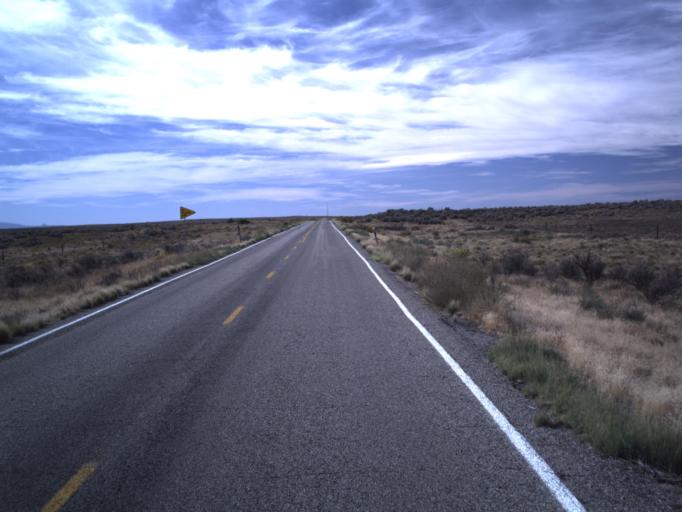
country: US
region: Utah
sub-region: San Juan County
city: Blanding
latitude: 37.3634
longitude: -109.3448
